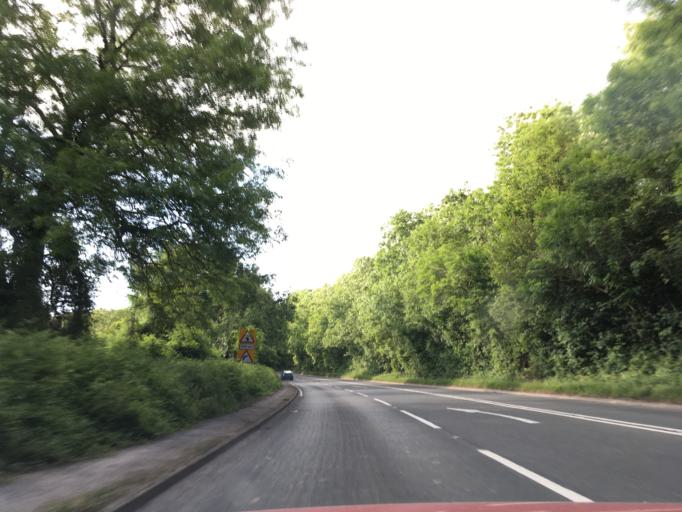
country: GB
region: England
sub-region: North Somerset
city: Winscombe
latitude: 51.2979
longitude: -2.8285
